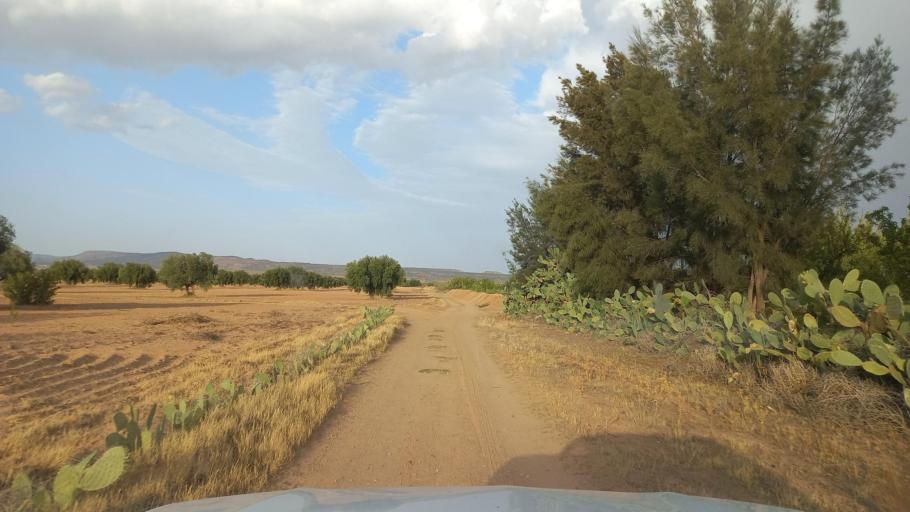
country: TN
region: Al Qasrayn
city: Sbiba
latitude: 35.2868
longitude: 9.0786
